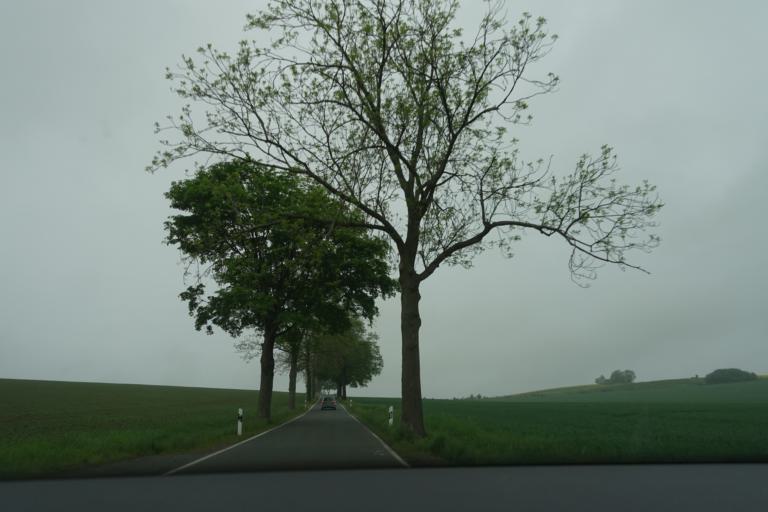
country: DE
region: Saxony
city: Grosshartmannsdorf
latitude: 50.8137
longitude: 13.2960
